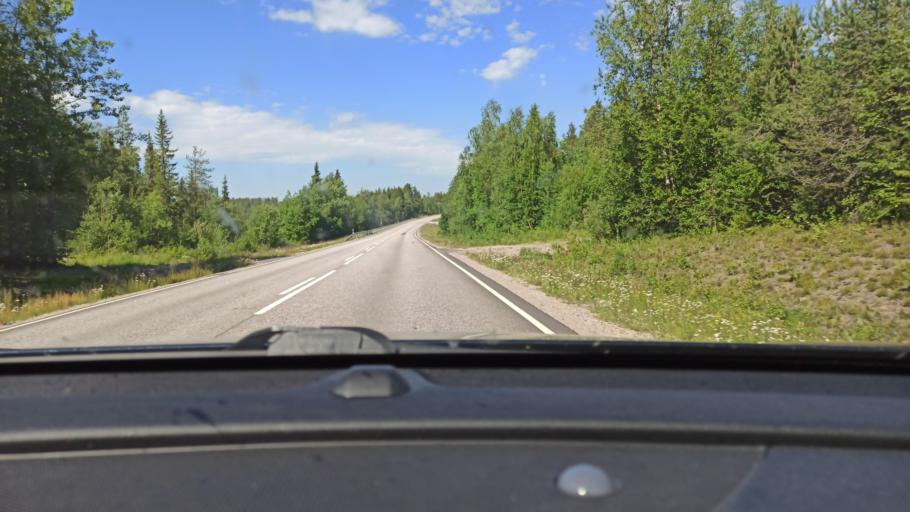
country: FI
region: Lapland
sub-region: Tunturi-Lappi
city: Muonio
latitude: 68.0086
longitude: 23.6002
